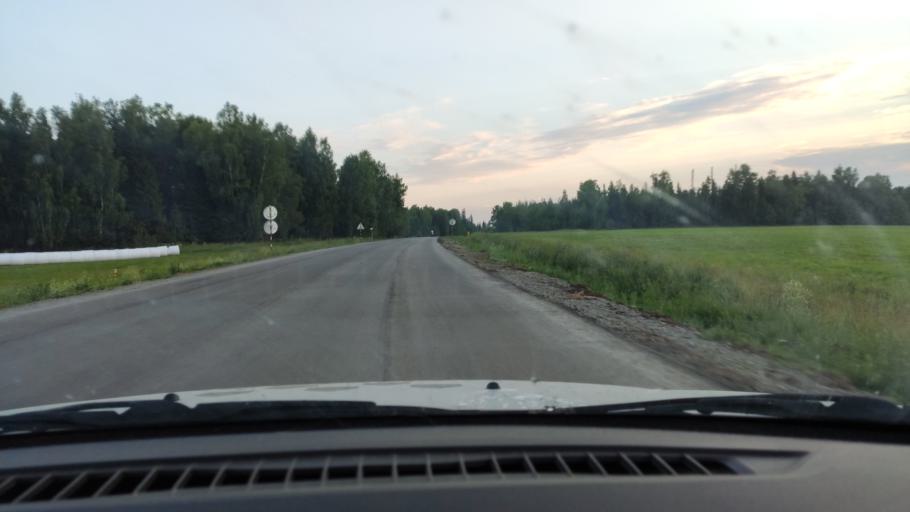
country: RU
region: Perm
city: Siva
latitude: 58.4623
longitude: 54.4075
